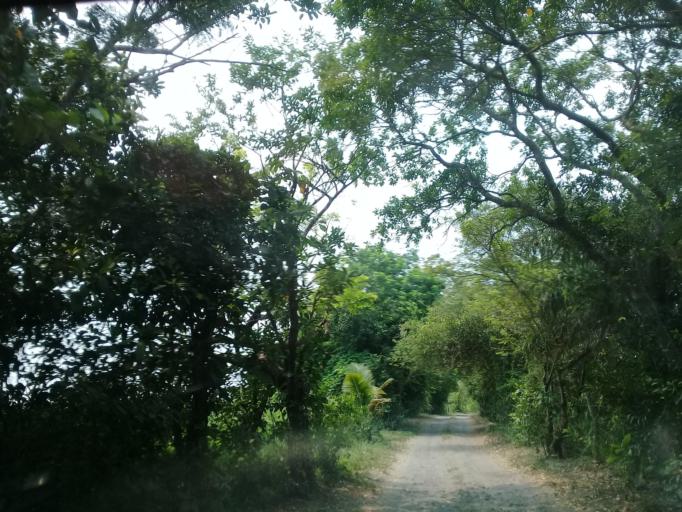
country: MX
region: Veracruz
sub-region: Veracruz
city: Hacienda Sotavento
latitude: 19.1389
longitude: -96.1587
